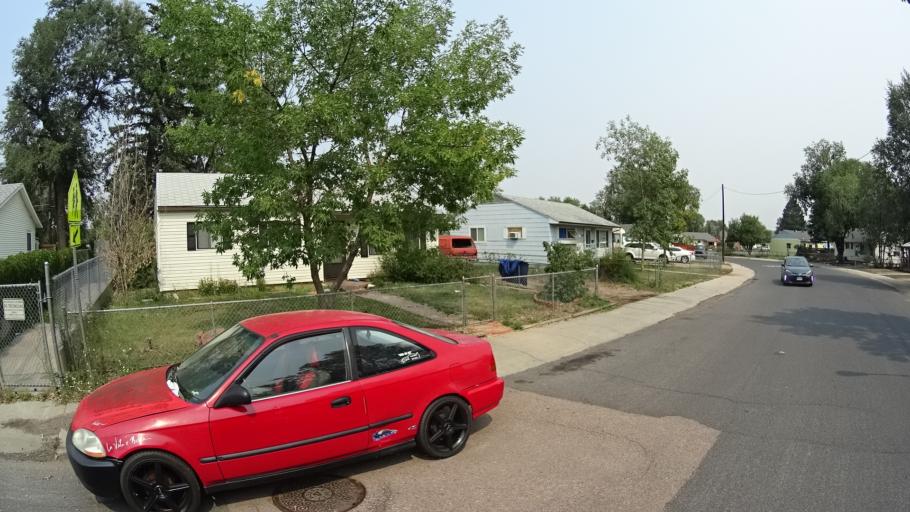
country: US
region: Colorado
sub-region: El Paso County
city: Colorado Springs
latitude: 38.8003
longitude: -104.8066
